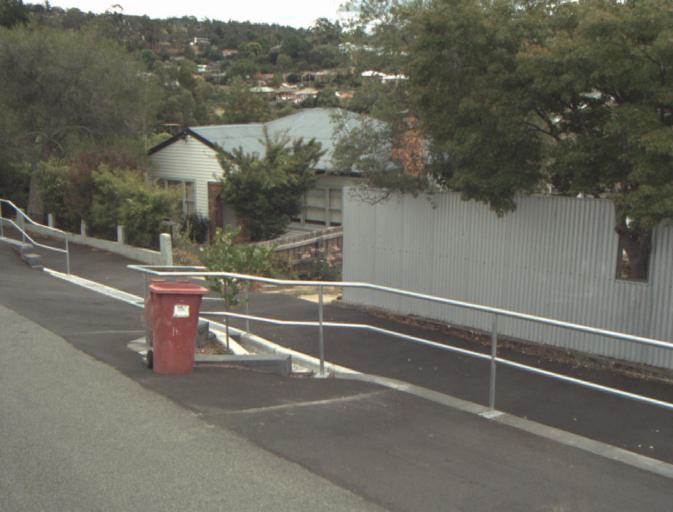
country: AU
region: Tasmania
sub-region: Launceston
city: Launceston
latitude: -41.4373
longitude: 147.1185
